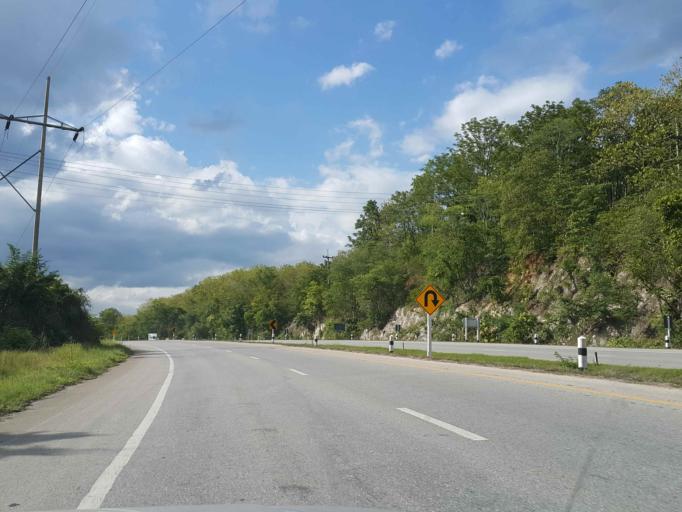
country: TH
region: Lampang
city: Thoen
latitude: 17.6962
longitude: 99.2331
